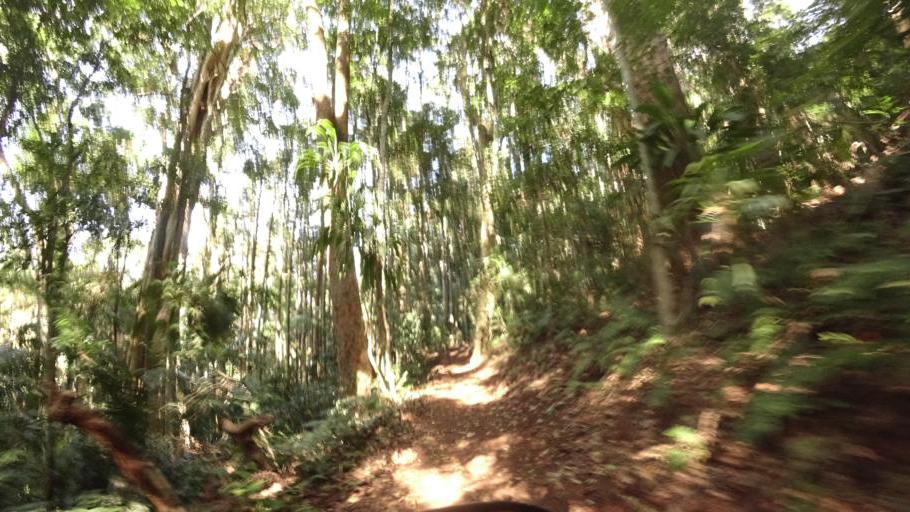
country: AU
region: Queensland
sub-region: Moreton Bay
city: Highvale
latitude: -27.4018
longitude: 152.7973
